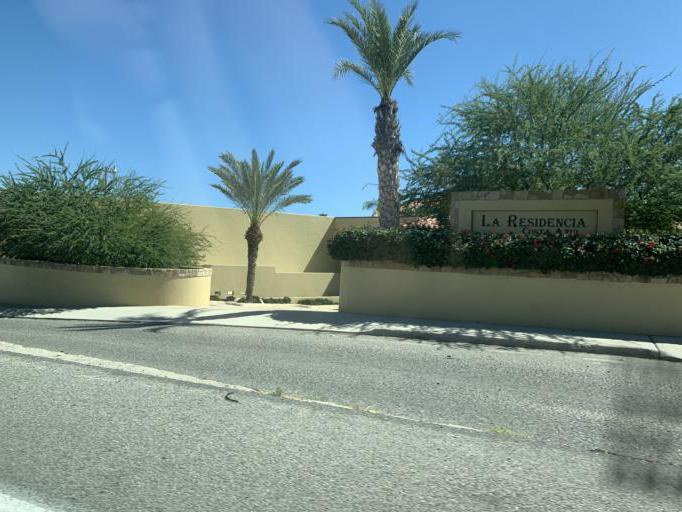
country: MX
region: Baja California Sur
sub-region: Los Cabos
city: San Jose del Cabo
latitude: 23.0282
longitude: -109.7162
